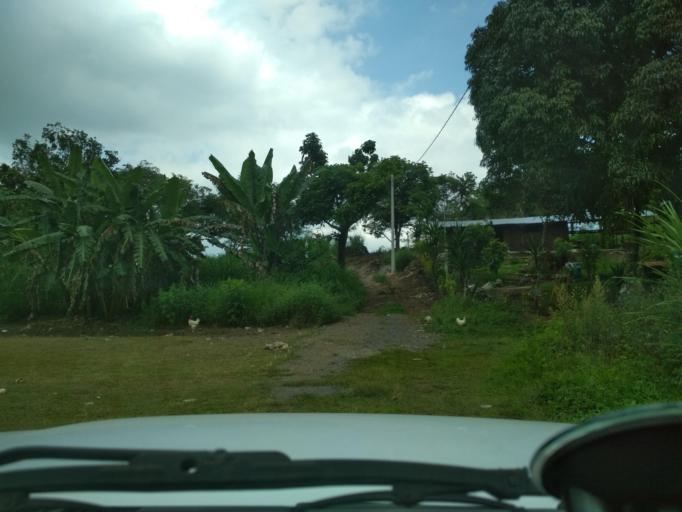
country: MX
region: Veracruz
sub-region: Ixtaczoquitlan
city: Buenavista
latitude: 18.8998
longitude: -97.0272
